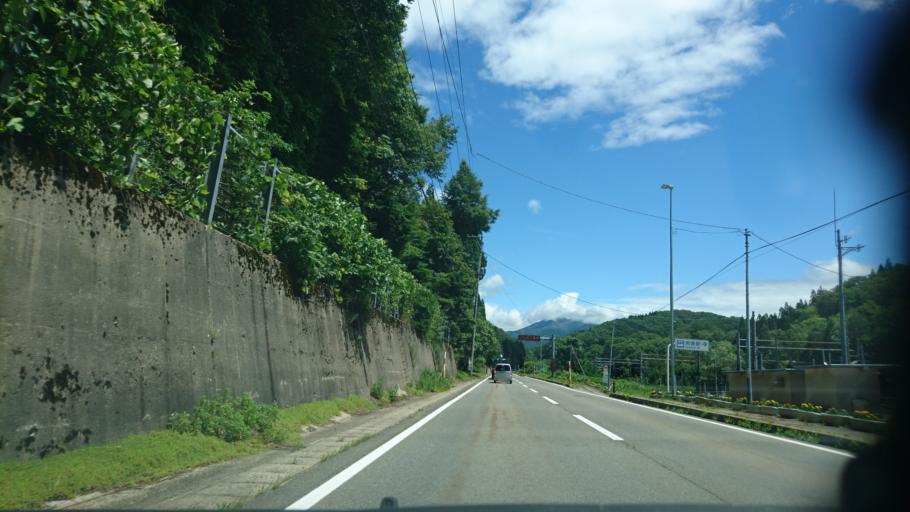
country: JP
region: Akita
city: Kakunodatemachi
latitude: 39.6692
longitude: 140.6922
